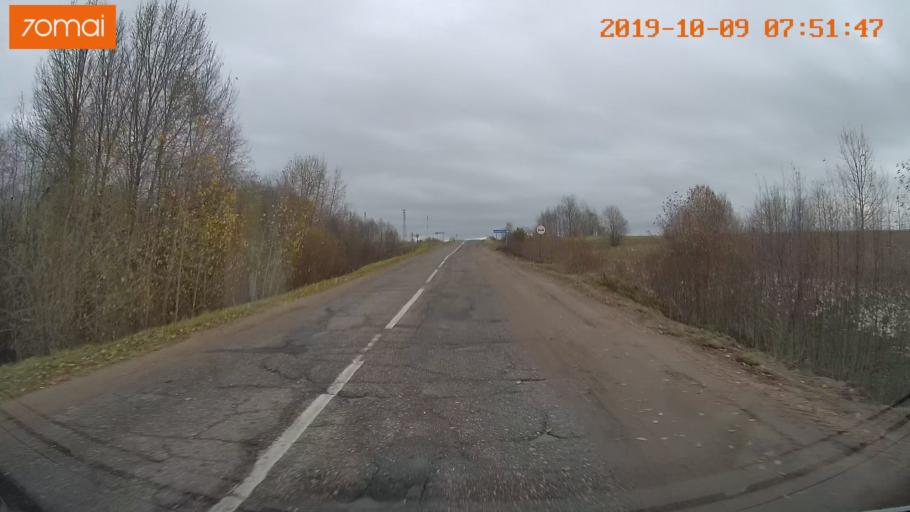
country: RU
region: Jaroslavl
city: Kukoboy
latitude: 58.6858
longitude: 39.8813
